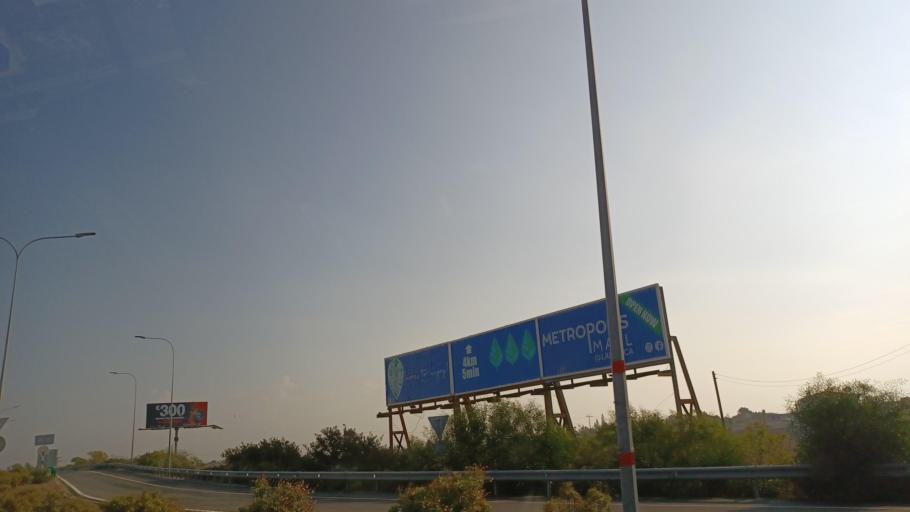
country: CY
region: Larnaka
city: Aradippou
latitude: 34.9525
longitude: 33.5739
